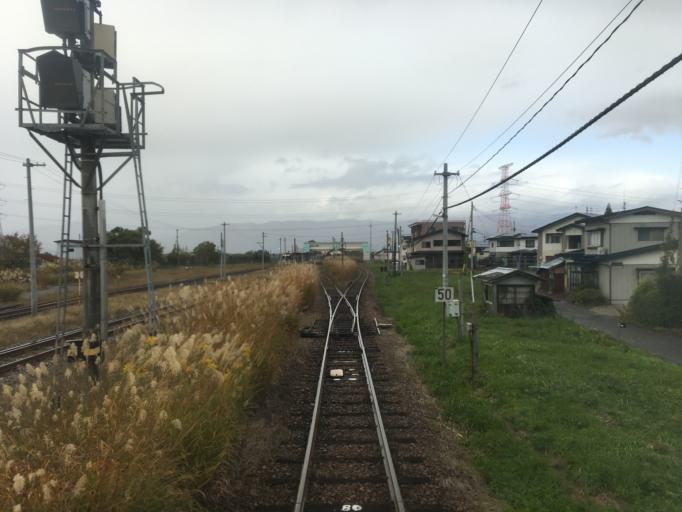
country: JP
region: Yamagata
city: Nagai
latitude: 38.0554
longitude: 140.0457
